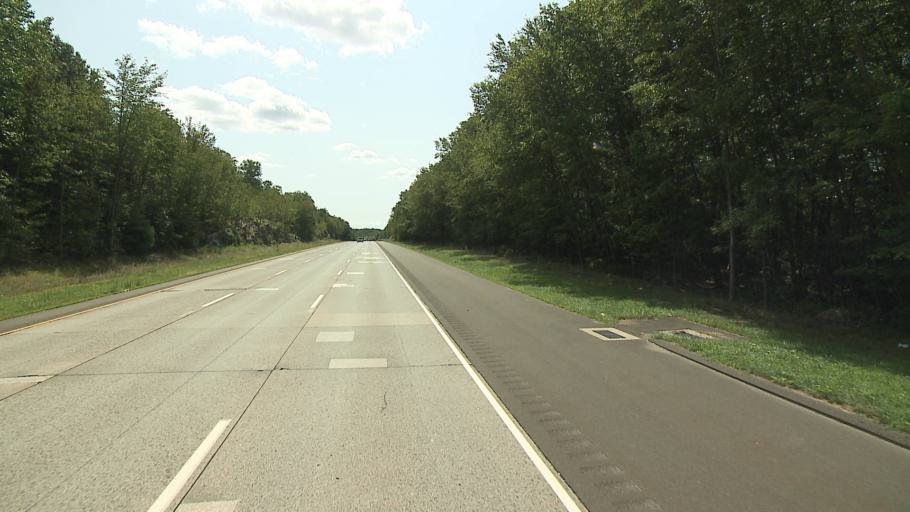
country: US
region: Connecticut
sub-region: Fairfield County
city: Trumbull
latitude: 41.2680
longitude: -73.2113
